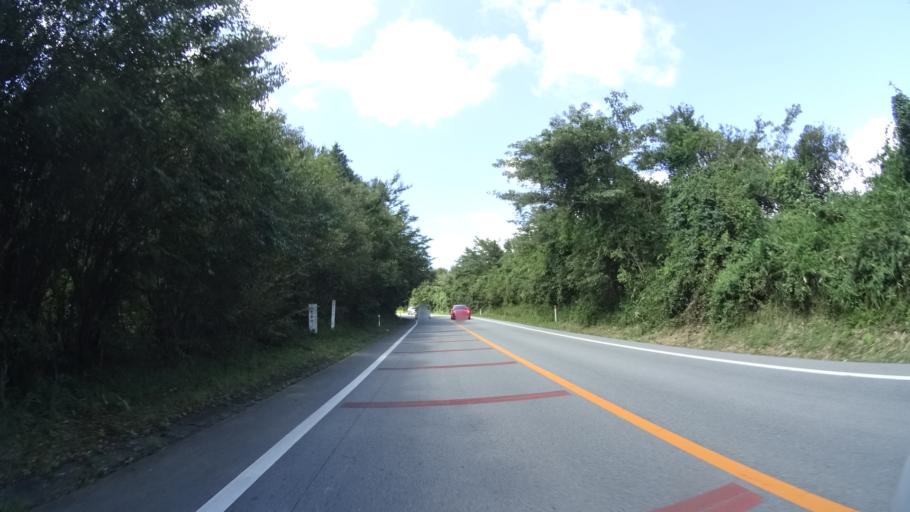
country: JP
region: Kumamoto
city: Aso
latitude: 33.0070
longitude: 131.1007
